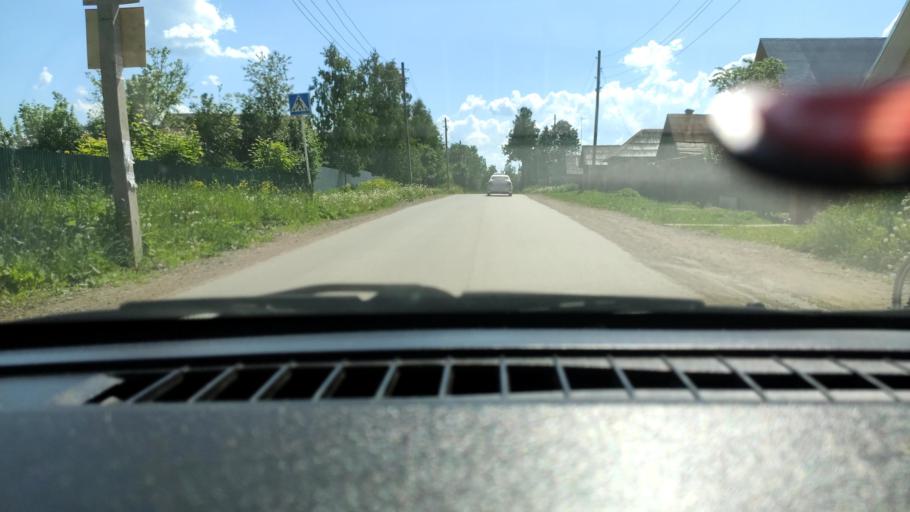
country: RU
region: Perm
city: Sylva
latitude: 58.0358
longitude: 56.7742
